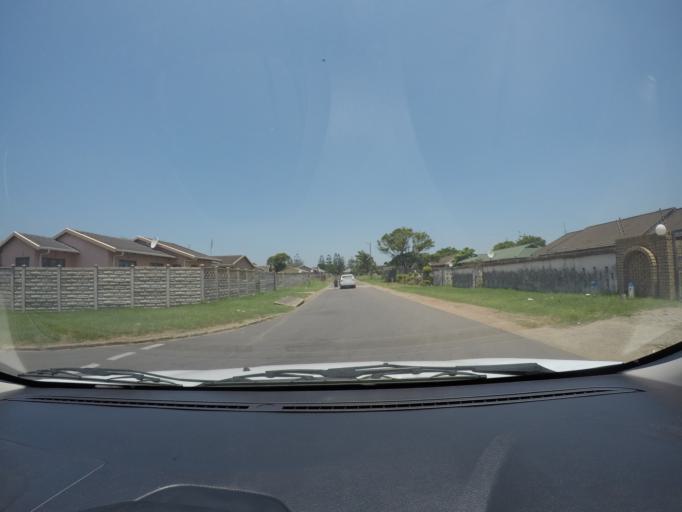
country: ZA
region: KwaZulu-Natal
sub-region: uThungulu District Municipality
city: eSikhawini
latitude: -28.8746
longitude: 31.8972
